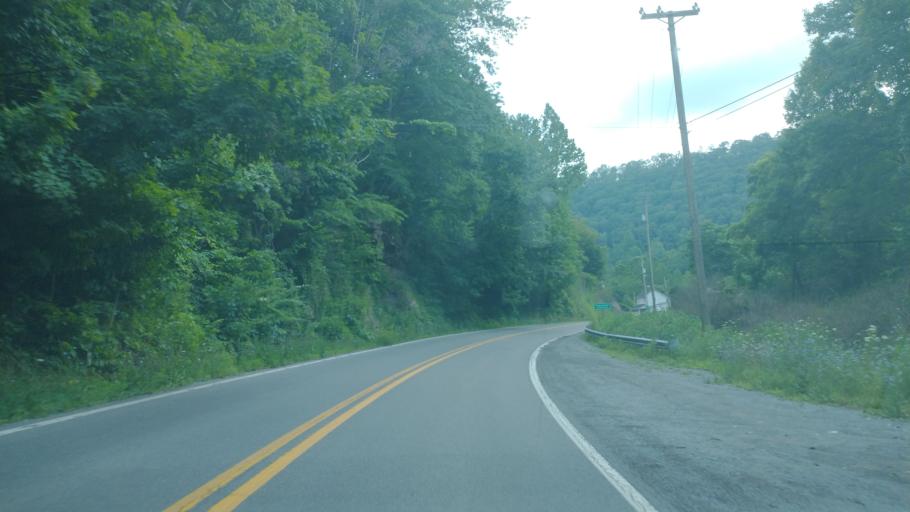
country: US
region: West Virginia
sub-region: McDowell County
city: Welch
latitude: 37.3981
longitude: -81.4223
